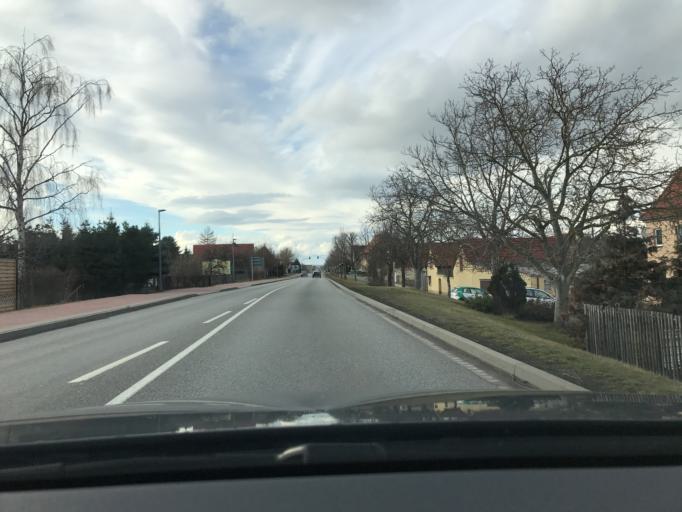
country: DE
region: Saxony-Anhalt
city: Roblingen am See
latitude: 51.4878
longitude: 11.6744
